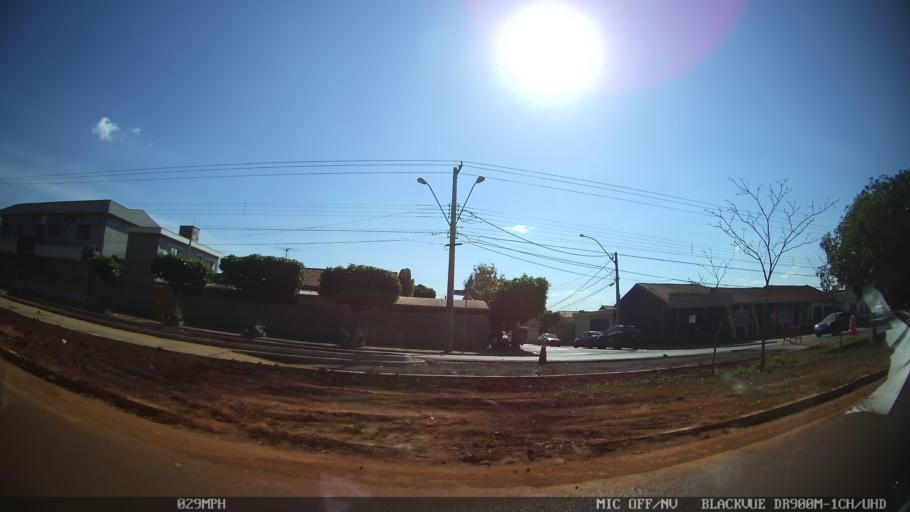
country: BR
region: Sao Paulo
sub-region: Ribeirao Preto
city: Ribeirao Preto
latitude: -21.1581
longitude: -47.7854
